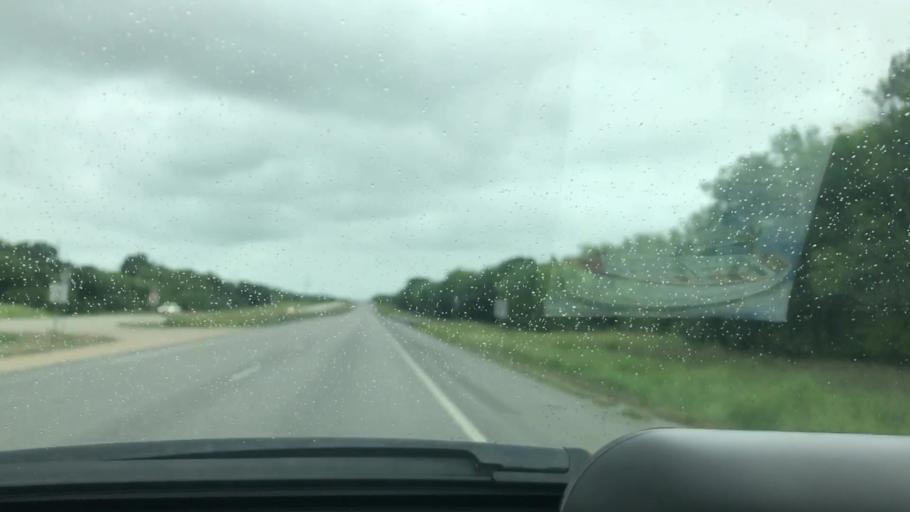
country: US
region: Oklahoma
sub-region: Coal County
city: Coalgate
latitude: 34.6169
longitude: -95.9674
